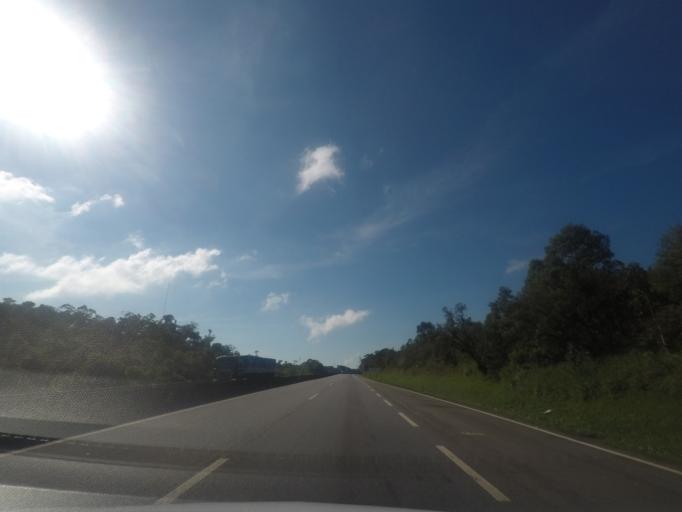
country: BR
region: Parana
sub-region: Piraquara
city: Piraquara
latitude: -25.5888
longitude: -48.9422
